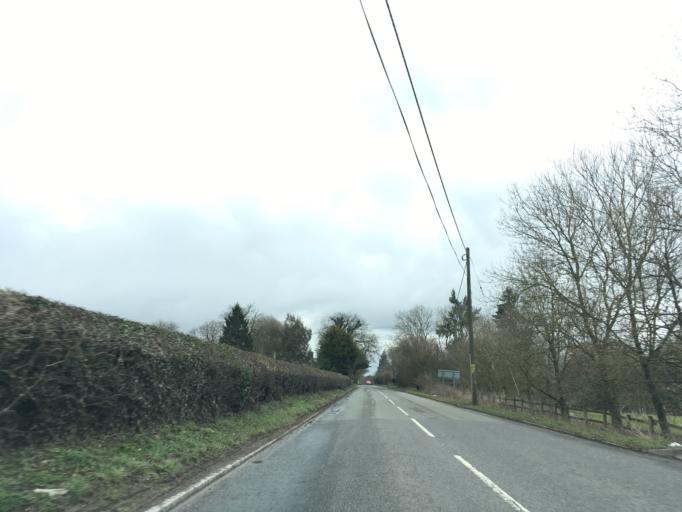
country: GB
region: England
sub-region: West Berkshire
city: Lambourn
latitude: 51.4838
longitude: -1.5503
